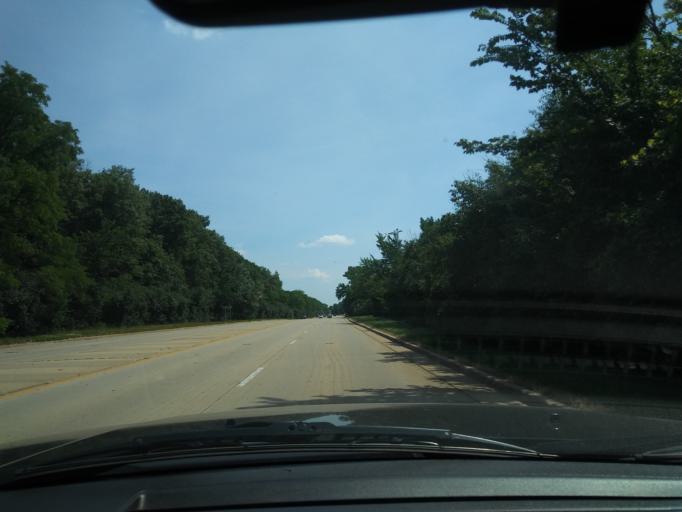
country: US
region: Illinois
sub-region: Cook County
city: Crestwood
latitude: 41.6306
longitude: -87.7766
